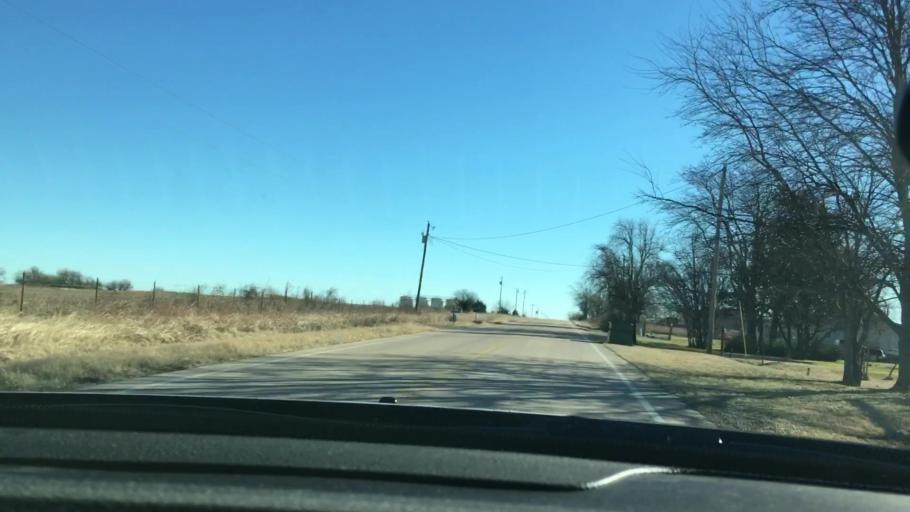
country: US
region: Oklahoma
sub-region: Marshall County
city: Madill
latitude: 34.1144
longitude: -96.7095
